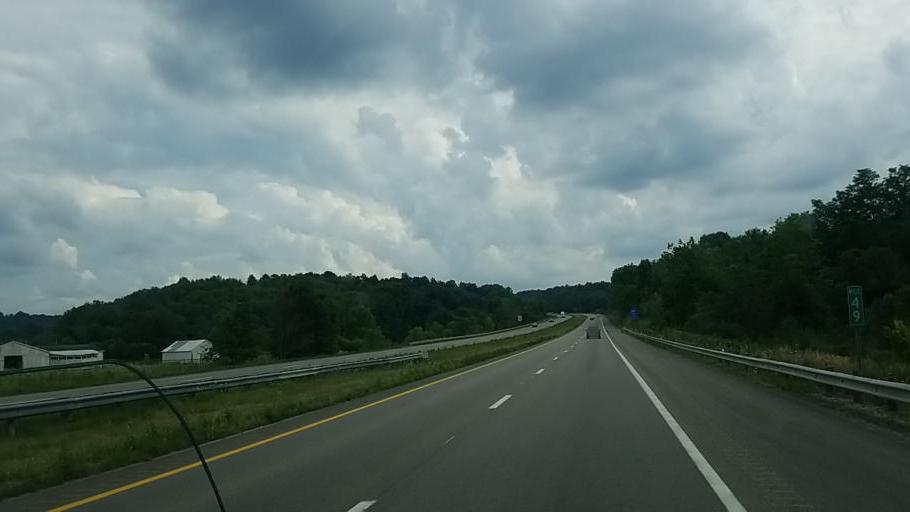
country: US
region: Ohio
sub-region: Guernsey County
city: Cambridge
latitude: 40.0670
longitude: -81.5673
